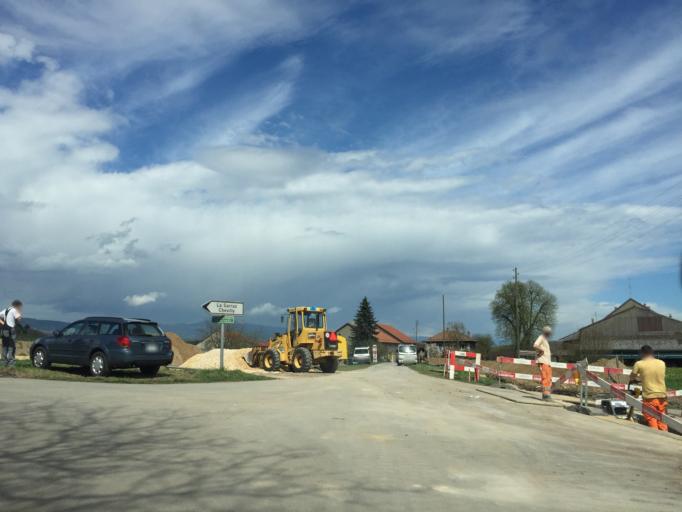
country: CH
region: Vaud
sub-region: Morges District
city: La Chaux
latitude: 46.6200
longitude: 6.4740
